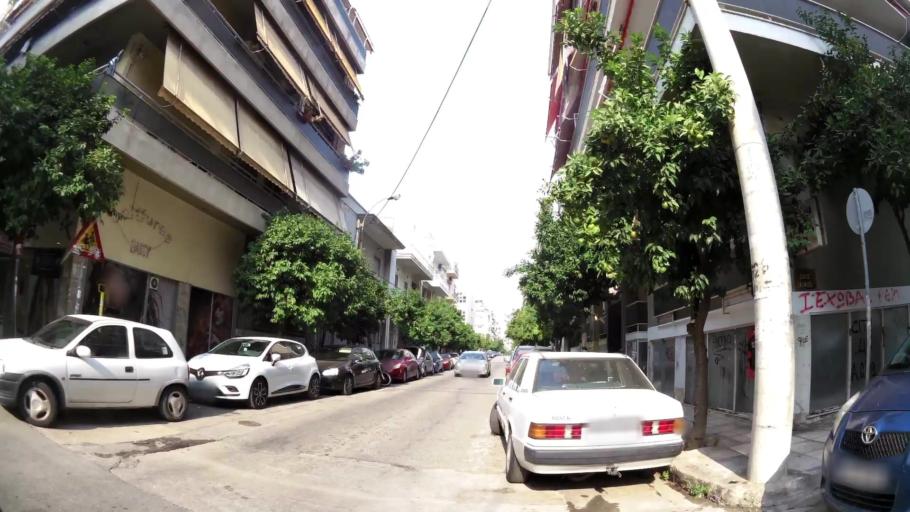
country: GR
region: Attica
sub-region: Nomarchia Athinas
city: Kallithea
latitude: 37.9557
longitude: 23.6988
